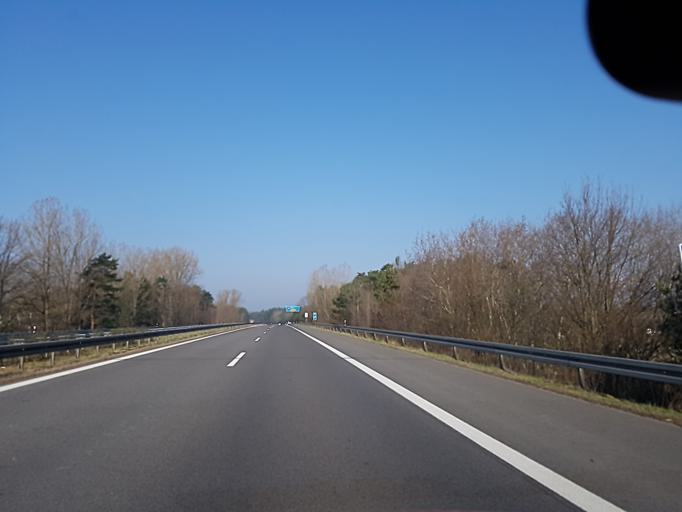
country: DE
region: Brandenburg
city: Forst
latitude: 51.7109
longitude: 14.6148
